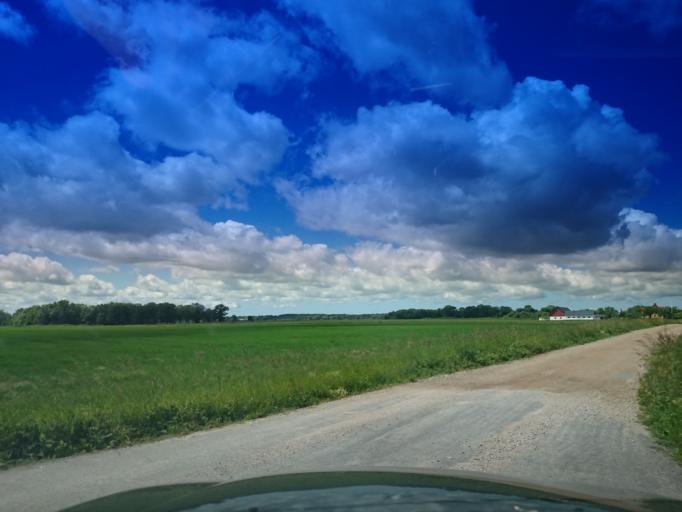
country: SE
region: Gotland
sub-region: Gotland
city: Hemse
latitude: 57.3381
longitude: 18.6333
